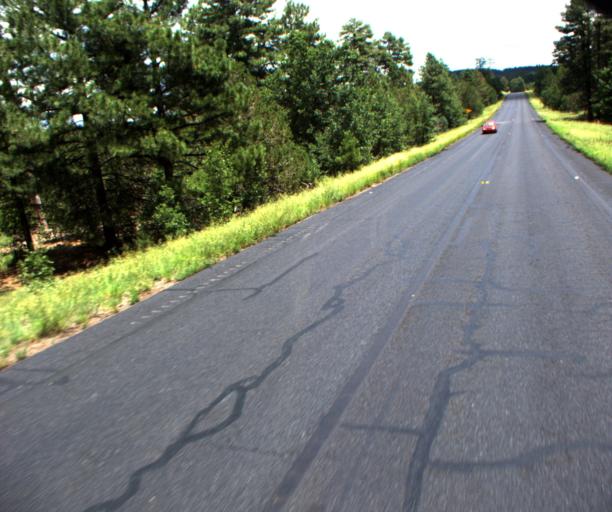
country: US
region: Arizona
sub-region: Gila County
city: Pine
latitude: 34.5203
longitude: -111.5180
